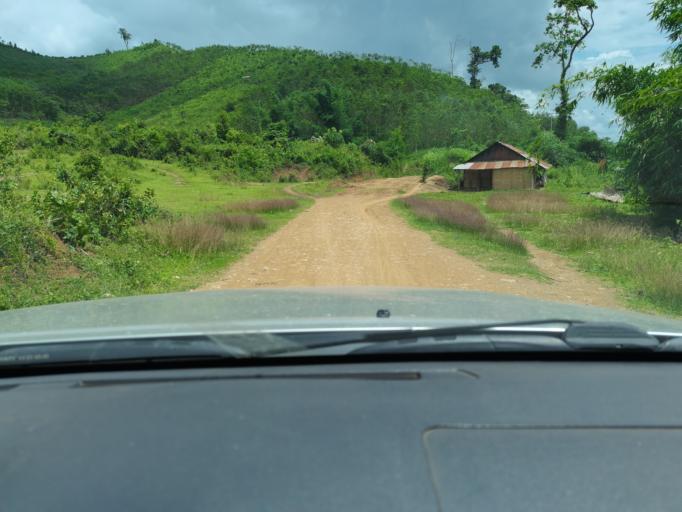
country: LA
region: Loungnamtha
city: Muang Long
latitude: 20.7218
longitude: 101.0142
